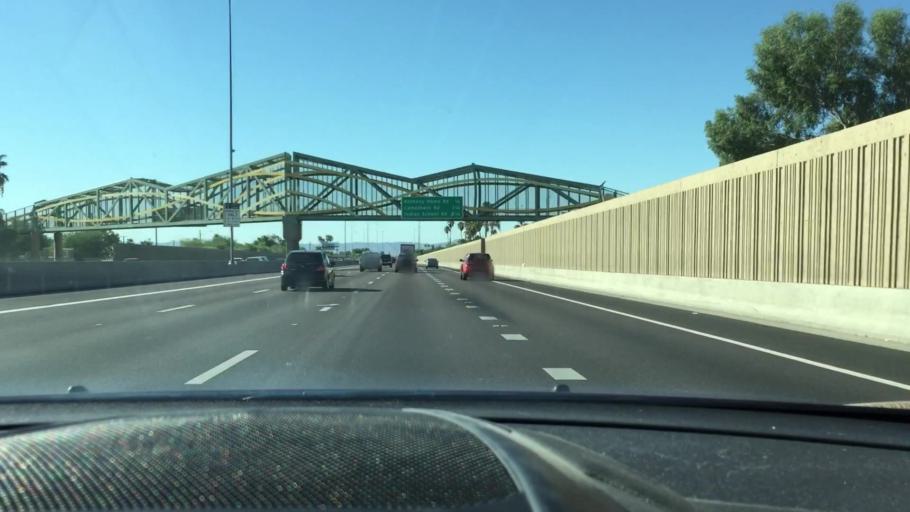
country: US
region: Arizona
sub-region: Maricopa County
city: Glendale
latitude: 33.5359
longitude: -112.1108
